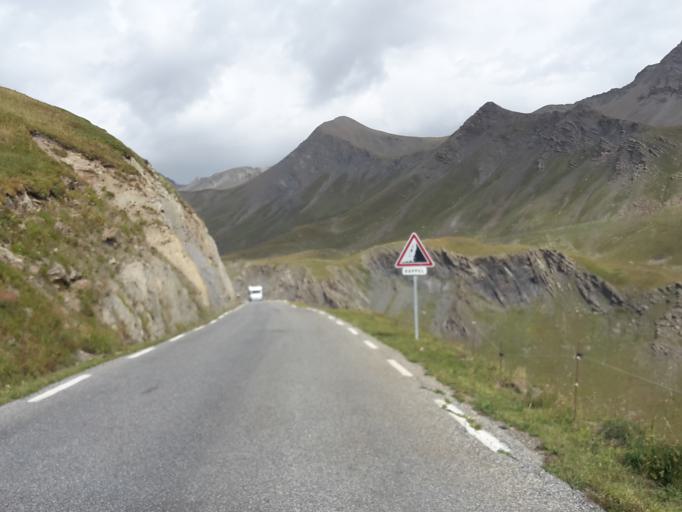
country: FR
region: Rhone-Alpes
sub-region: Departement de la Savoie
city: Valloire
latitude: 45.0456
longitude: 6.4003
